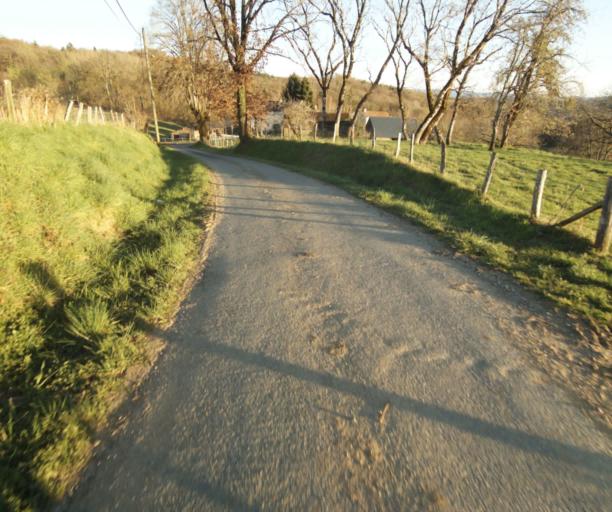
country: FR
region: Limousin
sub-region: Departement de la Correze
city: Saint-Clement
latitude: 45.3308
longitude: 1.7162
